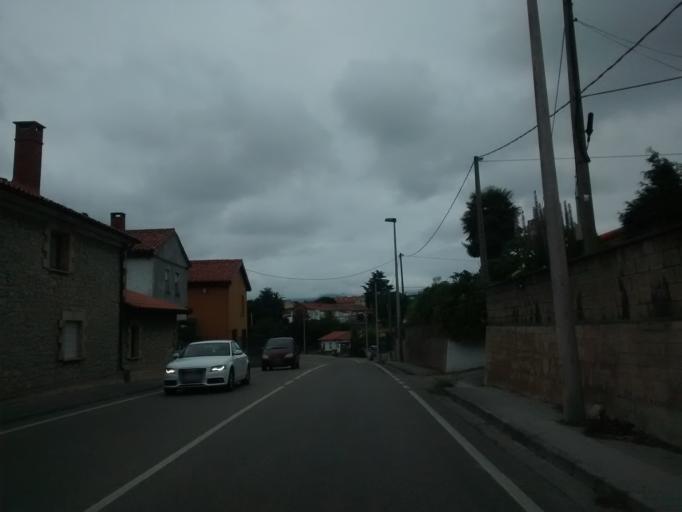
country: ES
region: Cantabria
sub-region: Provincia de Cantabria
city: Polanco
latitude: 43.3831
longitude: -4.0486
